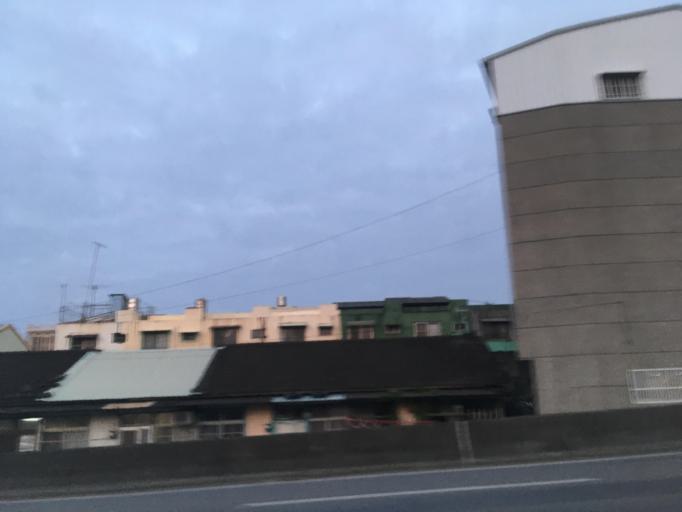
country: TW
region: Taiwan
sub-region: Chiayi
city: Jiayi Shi
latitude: 23.5994
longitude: 120.4516
